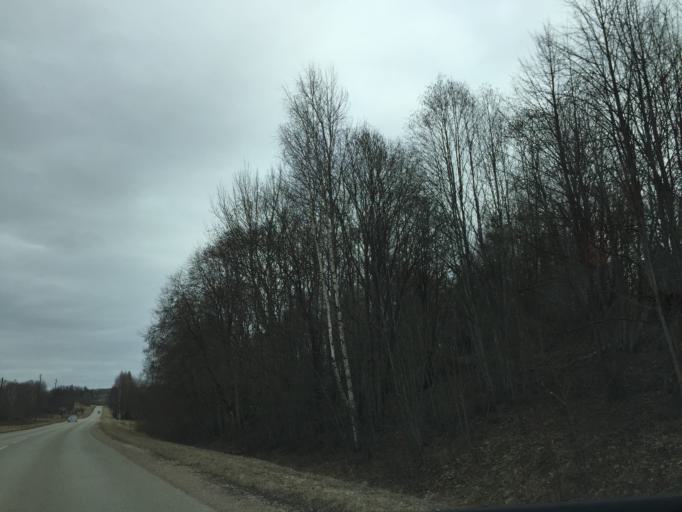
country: LV
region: Kraslavas Rajons
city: Kraslava
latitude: 55.9612
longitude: 27.1642
